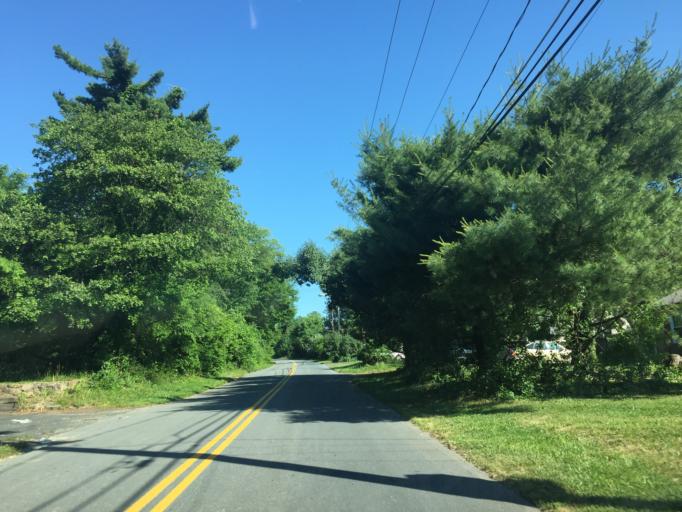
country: US
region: Maryland
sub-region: Harford County
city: Joppatowne
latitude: 39.4606
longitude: -76.3613
